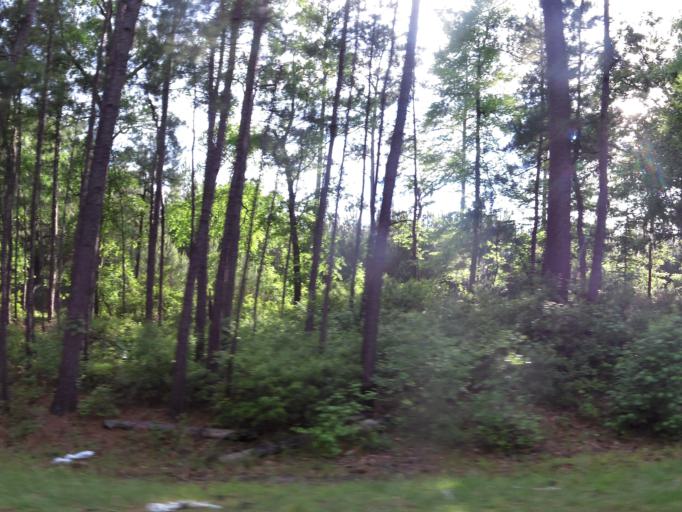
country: US
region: South Carolina
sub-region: Jasper County
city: Ridgeland
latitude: 32.5418
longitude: -81.1603
